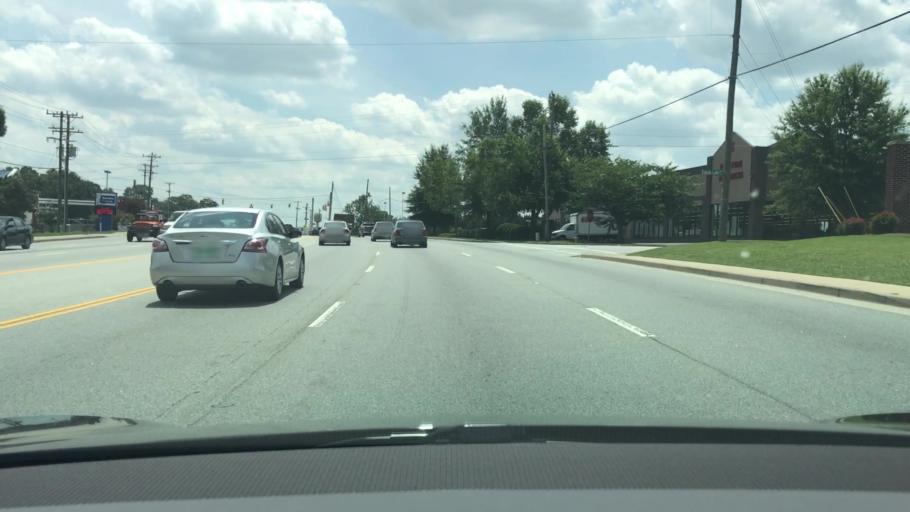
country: US
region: South Carolina
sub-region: Greenville County
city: Berea
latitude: 34.8696
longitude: -82.4666
